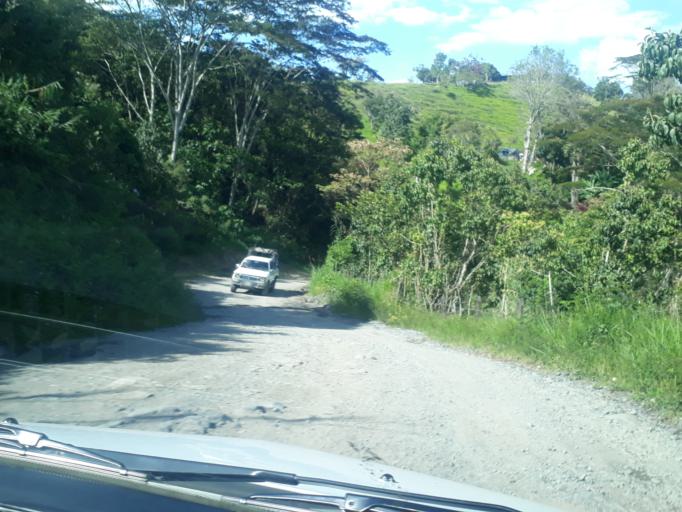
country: CO
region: Santander
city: Velez
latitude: 6.0524
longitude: -73.6507
